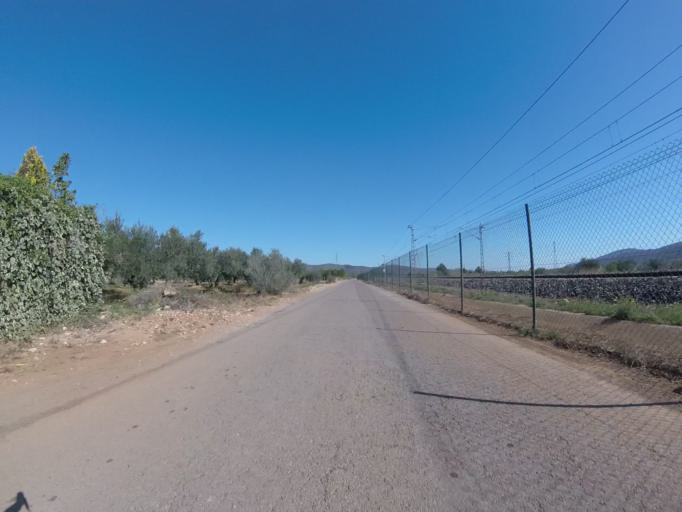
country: ES
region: Valencia
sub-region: Provincia de Castello
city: Alcala de Xivert
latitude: 40.3157
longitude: 0.2330
